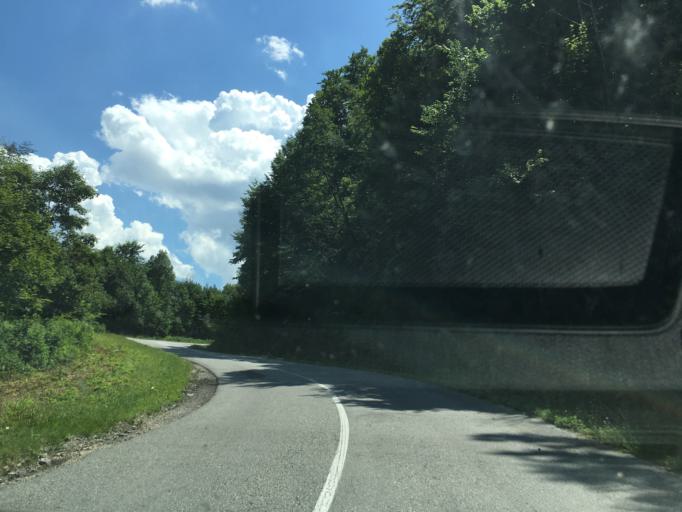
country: RS
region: Central Serbia
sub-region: Kolubarski Okrug
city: Mionica
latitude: 44.1425
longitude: 20.0177
